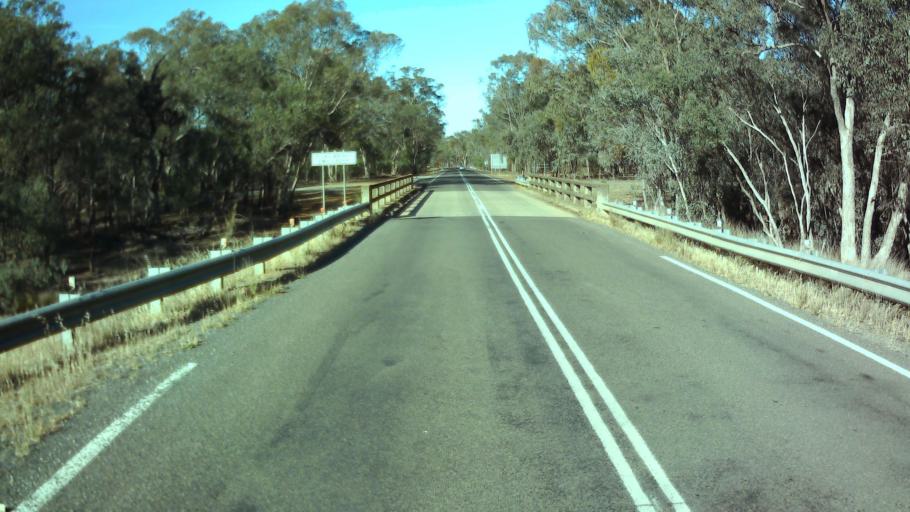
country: AU
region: New South Wales
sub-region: Weddin
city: Grenfell
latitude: -34.0008
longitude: 148.1300
